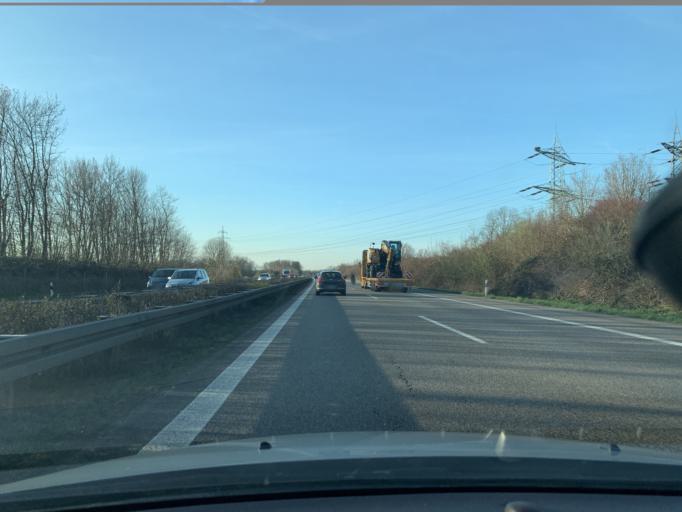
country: DE
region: Baden-Wuerttemberg
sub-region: Freiburg Region
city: Vorstetten
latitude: 48.0771
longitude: 7.8063
